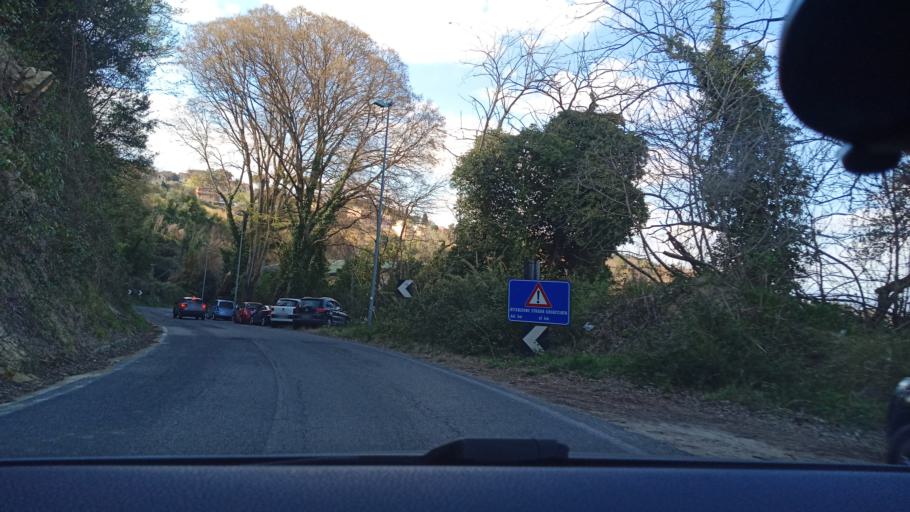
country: IT
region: Latium
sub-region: Citta metropolitana di Roma Capitale
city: Torrita Tiberina
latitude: 42.2391
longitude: 12.6182
